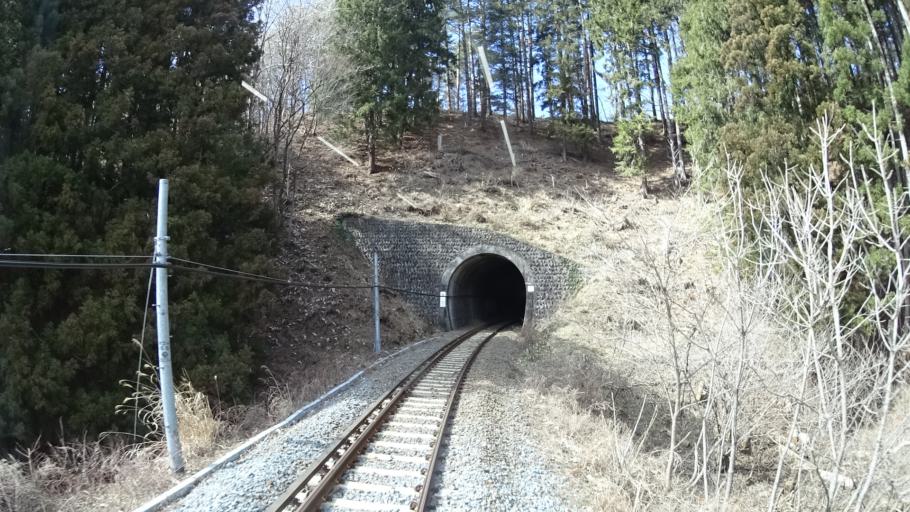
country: JP
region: Iwate
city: Yamada
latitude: 39.4762
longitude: 141.9257
